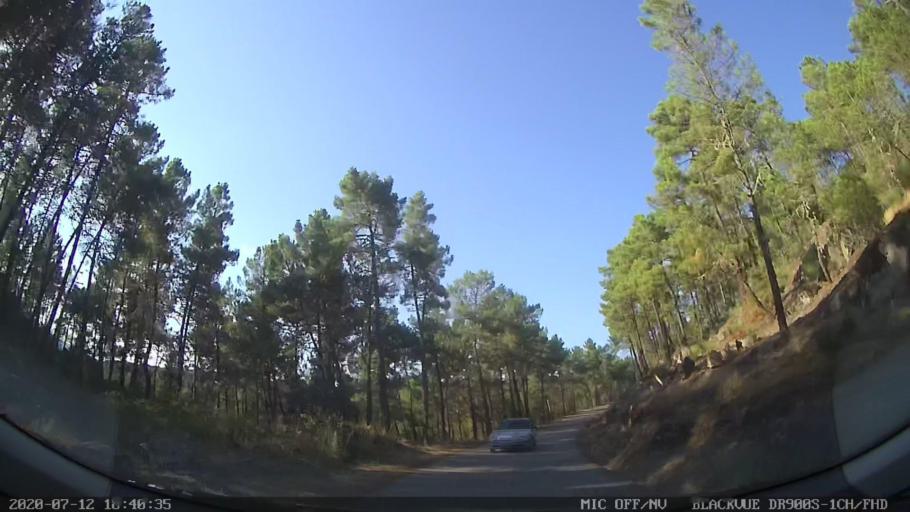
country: PT
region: Viseu
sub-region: Sao Joao da Pesqueira
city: Sao Joao da Pesqueira
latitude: 41.2516
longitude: -7.4272
